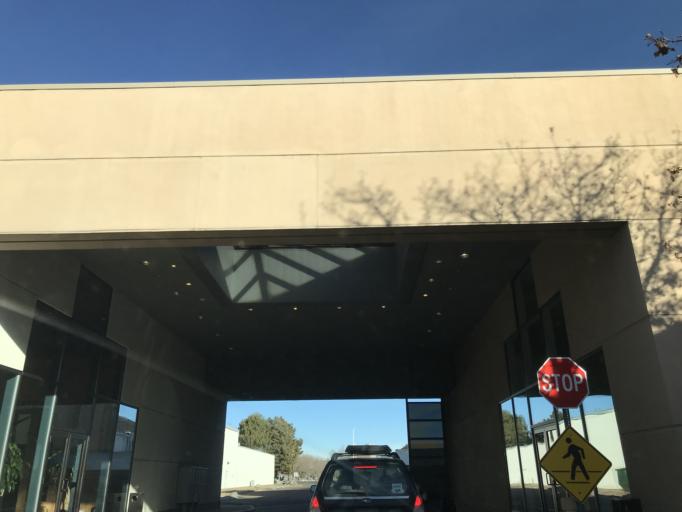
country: US
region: Colorado
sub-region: Denver County
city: Denver
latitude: 39.7062
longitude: -104.9899
